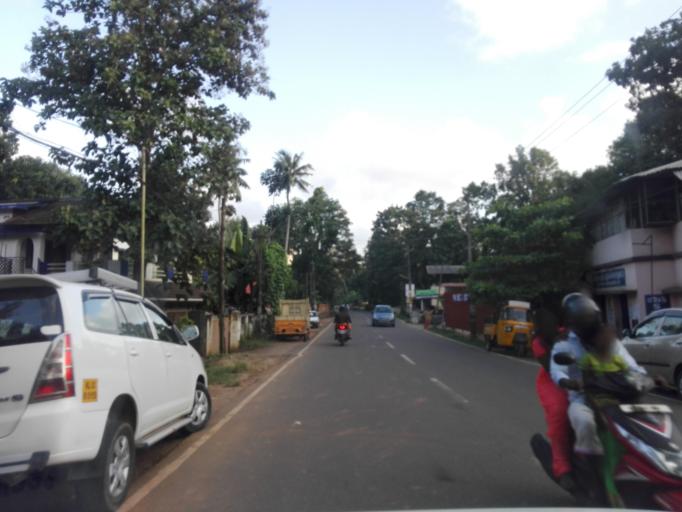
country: IN
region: Kerala
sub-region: Kottayam
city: Kottayam
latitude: 9.6118
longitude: 76.5076
